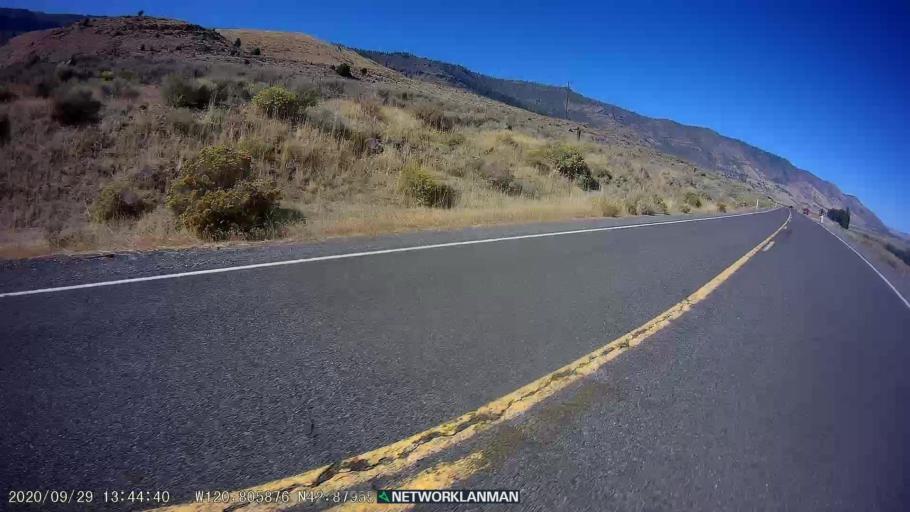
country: US
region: Oregon
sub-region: Lake County
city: Lakeview
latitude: 42.8796
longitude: -120.8058
